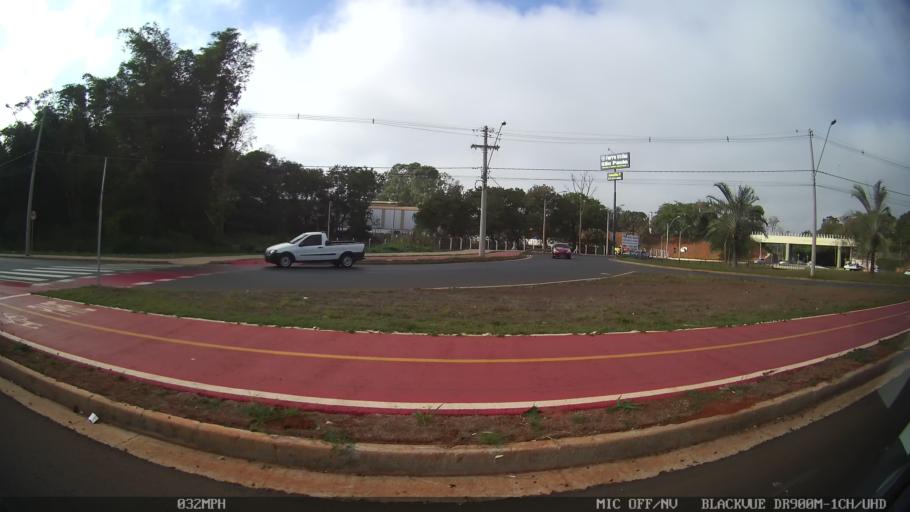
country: BR
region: Sao Paulo
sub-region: Sao Jose Do Rio Preto
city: Sao Jose do Rio Preto
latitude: -20.8138
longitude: -49.4345
